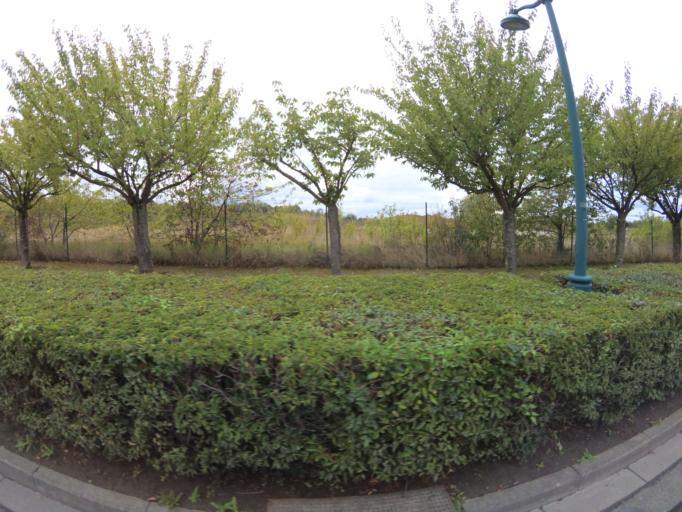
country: FR
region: Ile-de-France
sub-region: Departement de Seine-et-Marne
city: Serris
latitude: 48.8636
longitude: 2.7884
